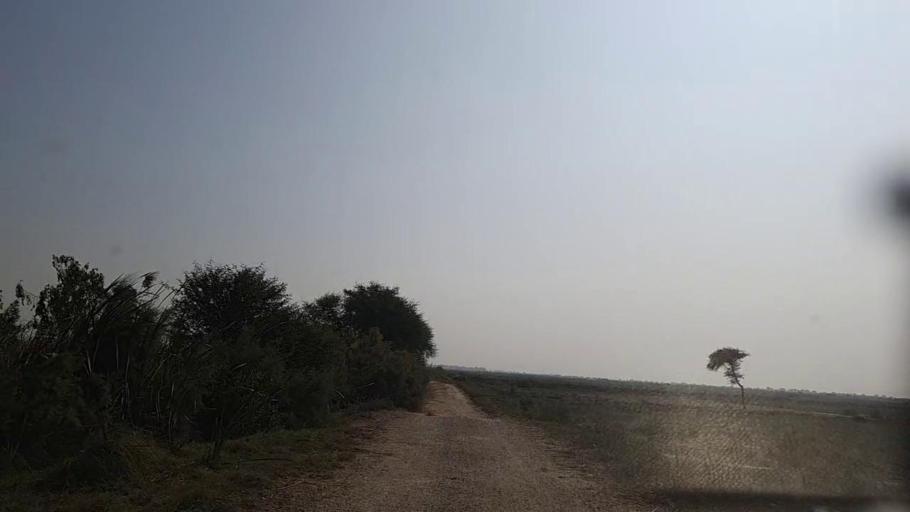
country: PK
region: Sindh
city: Mirpur Batoro
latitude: 24.5677
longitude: 68.2197
